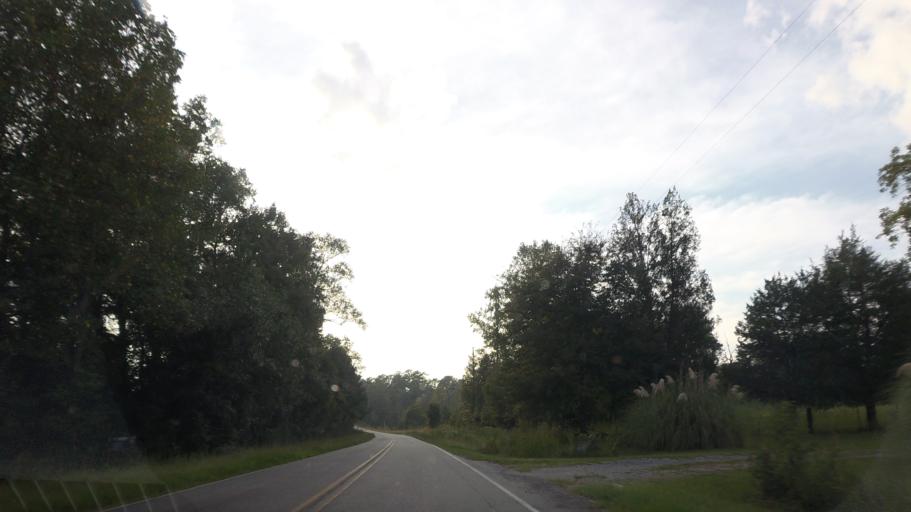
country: US
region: Georgia
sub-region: Bibb County
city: Macon
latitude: 32.8733
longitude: -83.4952
